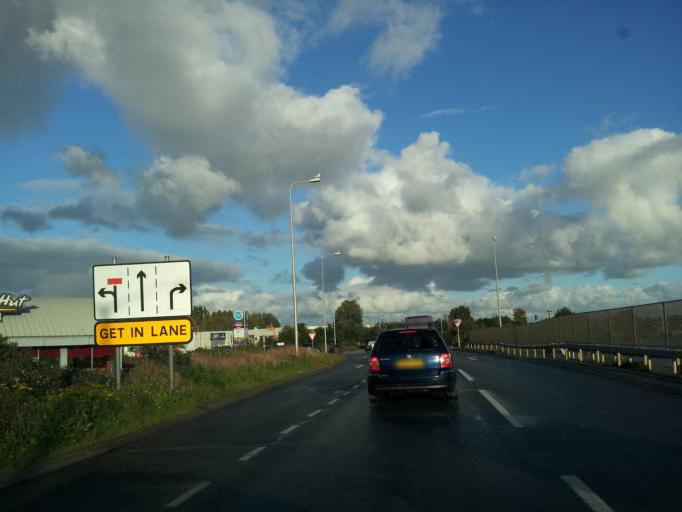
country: GB
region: England
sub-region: Norfolk
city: Great Yarmouth
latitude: 52.5979
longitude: 1.7142
